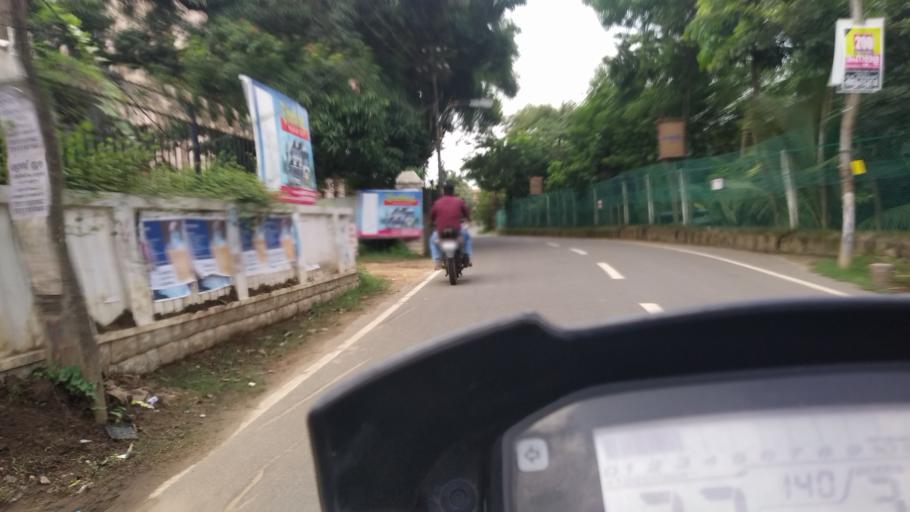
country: IN
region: Kerala
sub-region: Ernakulam
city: Aluva
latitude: 10.1144
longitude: 76.3478
